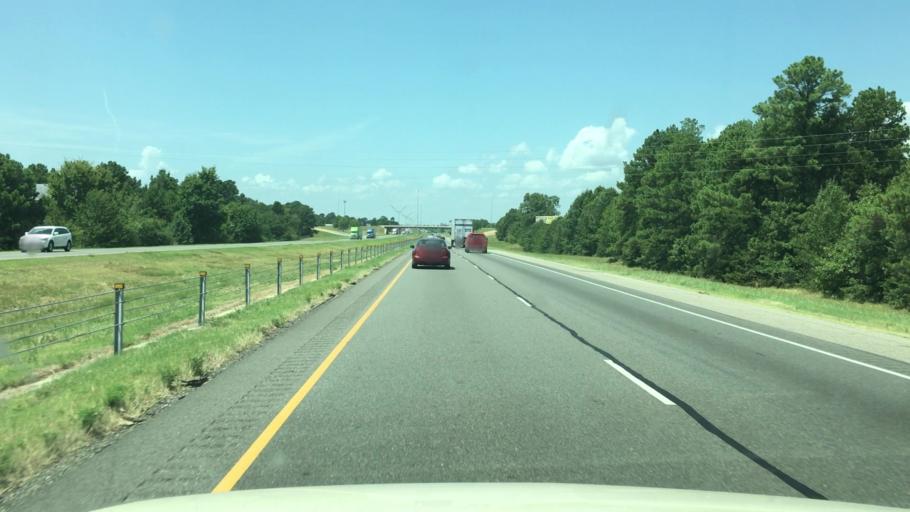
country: US
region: Arkansas
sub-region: Miller County
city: Texarkana
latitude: 33.4775
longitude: -93.9991
